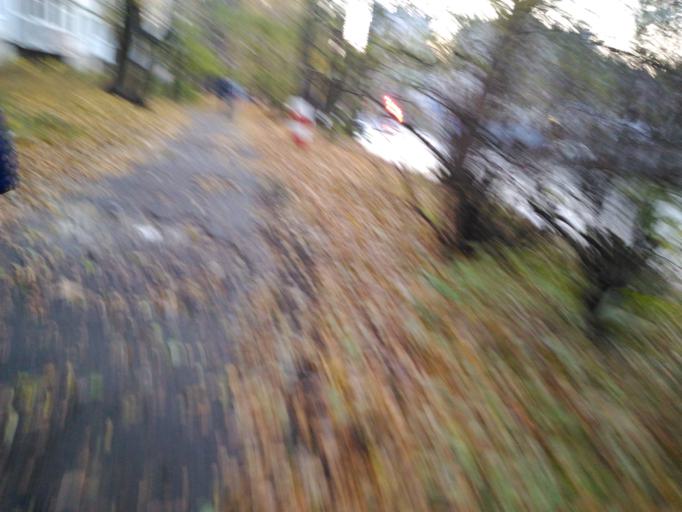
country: RU
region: Ulyanovsk
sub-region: Ulyanovskiy Rayon
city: Ulyanovsk
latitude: 54.3233
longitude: 48.3850
